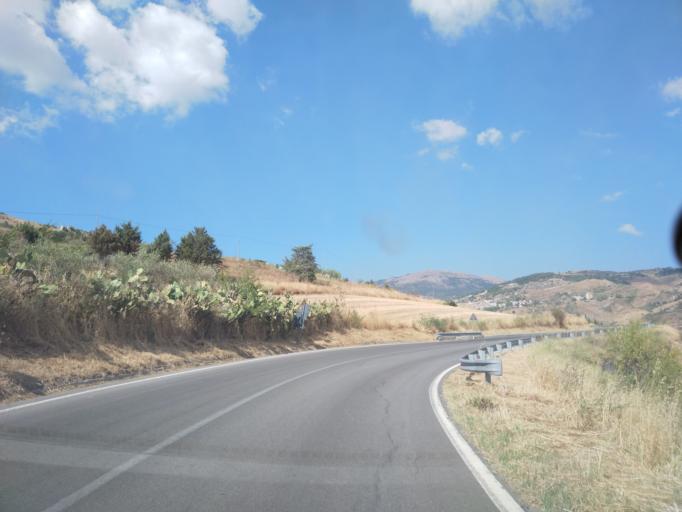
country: IT
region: Sicily
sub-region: Palermo
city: Petralia Sottana
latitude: 37.7895
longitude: 14.0747
